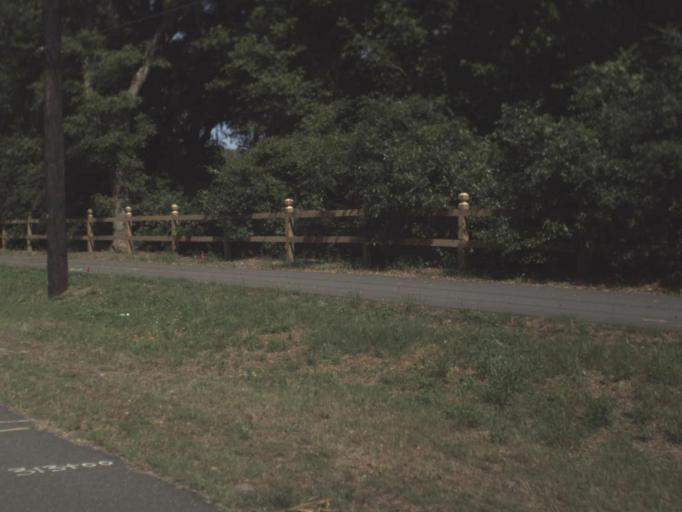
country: US
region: Florida
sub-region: Nassau County
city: Fernandina Beach
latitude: 30.5967
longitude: -81.4504
